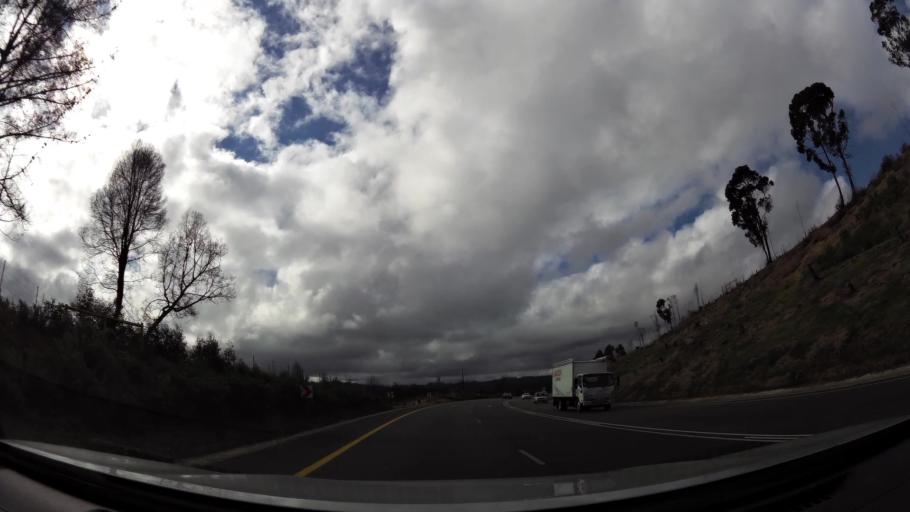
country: ZA
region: Western Cape
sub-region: Eden District Municipality
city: Knysna
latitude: -34.0358
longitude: 23.1237
